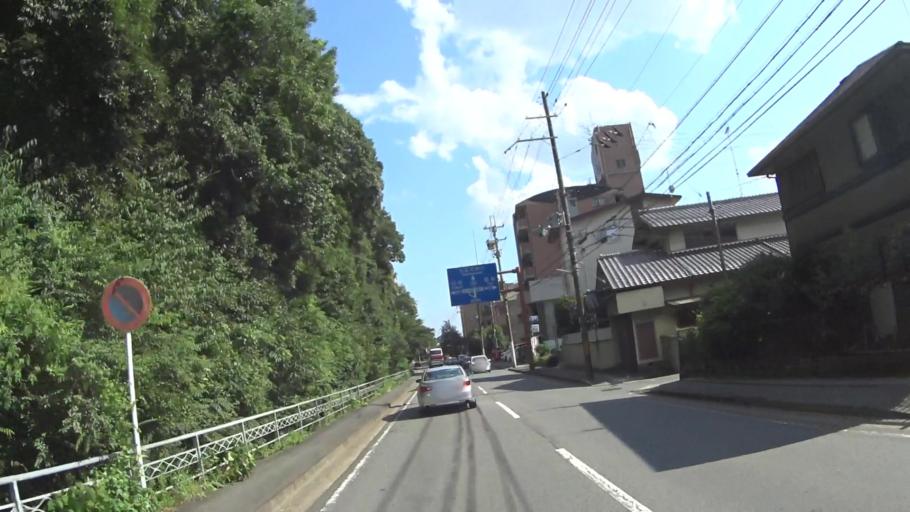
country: JP
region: Kyoto
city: Kyoto
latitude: 35.0214
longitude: 135.7121
